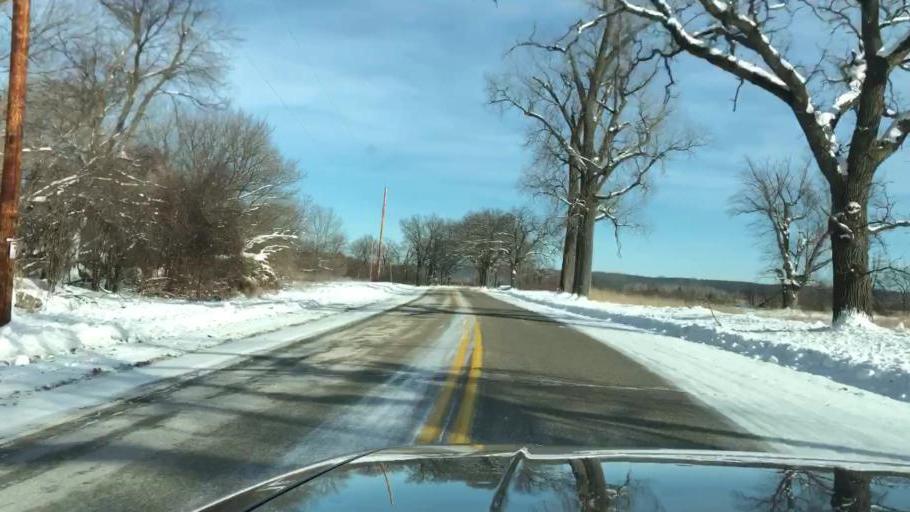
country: US
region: Wisconsin
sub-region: Waukesha County
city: Eagle
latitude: 42.9300
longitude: -88.4923
